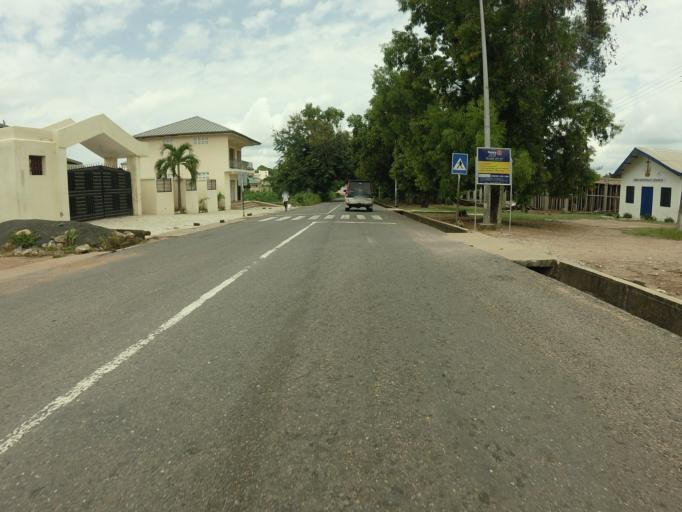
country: GH
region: Volta
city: Ho
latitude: 6.5996
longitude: 0.4624
